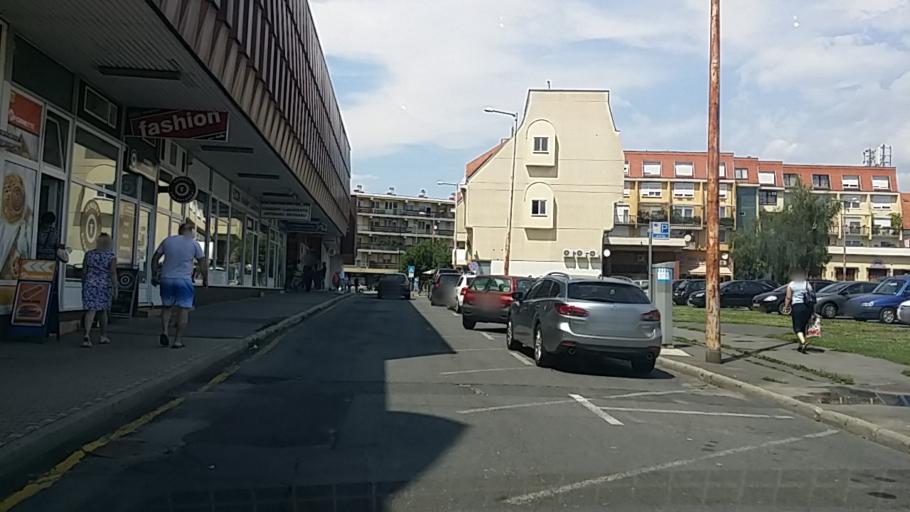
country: HU
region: Zala
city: Nagykanizsa
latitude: 46.4540
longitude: 16.9877
